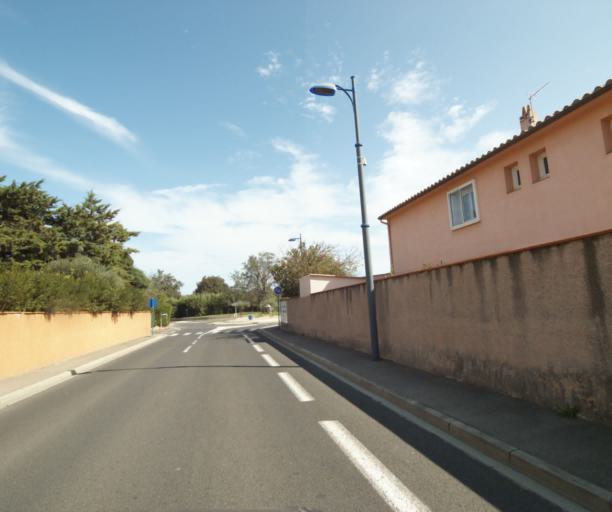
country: FR
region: Languedoc-Roussillon
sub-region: Departement des Pyrenees-Orientales
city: Argelers
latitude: 42.5504
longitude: 3.0243
